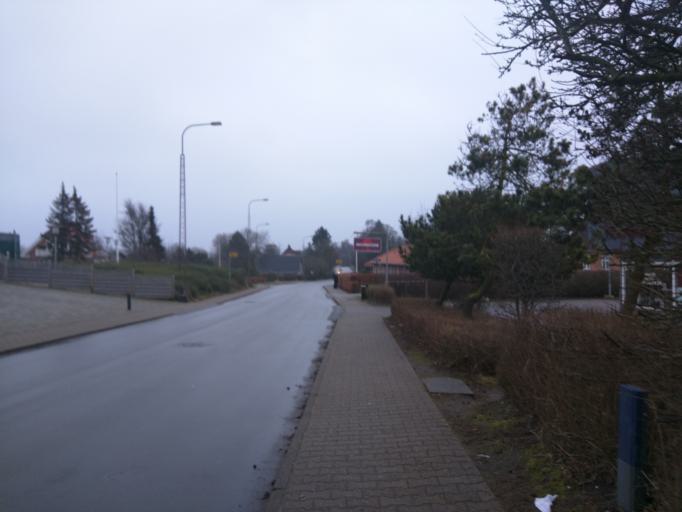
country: DK
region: South Denmark
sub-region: Fredericia Kommune
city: Snoghoj
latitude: 55.5460
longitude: 9.7100
